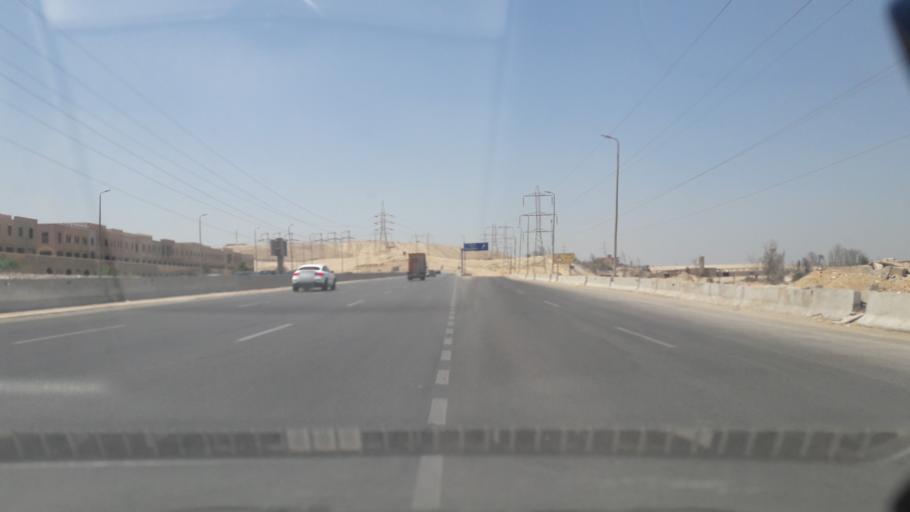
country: EG
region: Al Jizah
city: Awsim
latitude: 30.0208
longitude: 31.0818
